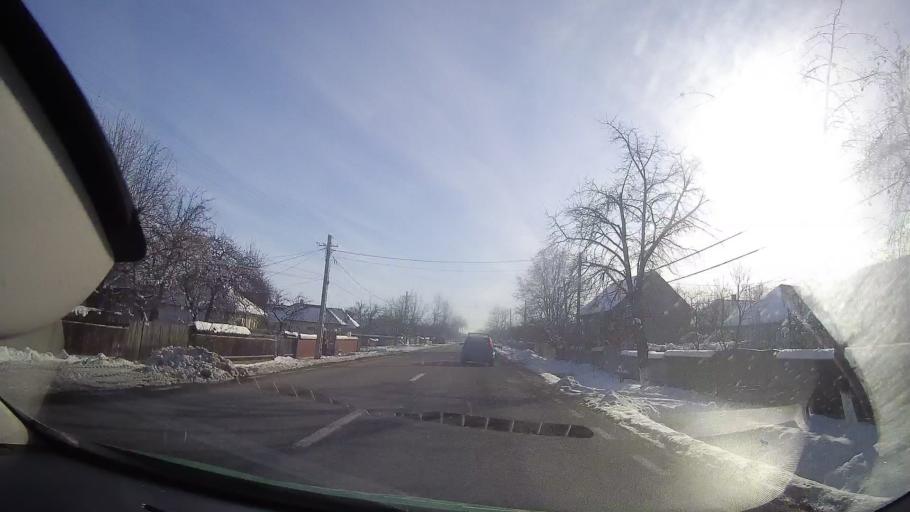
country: RO
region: Neamt
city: Bodesti
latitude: 47.0412
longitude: 26.4072
